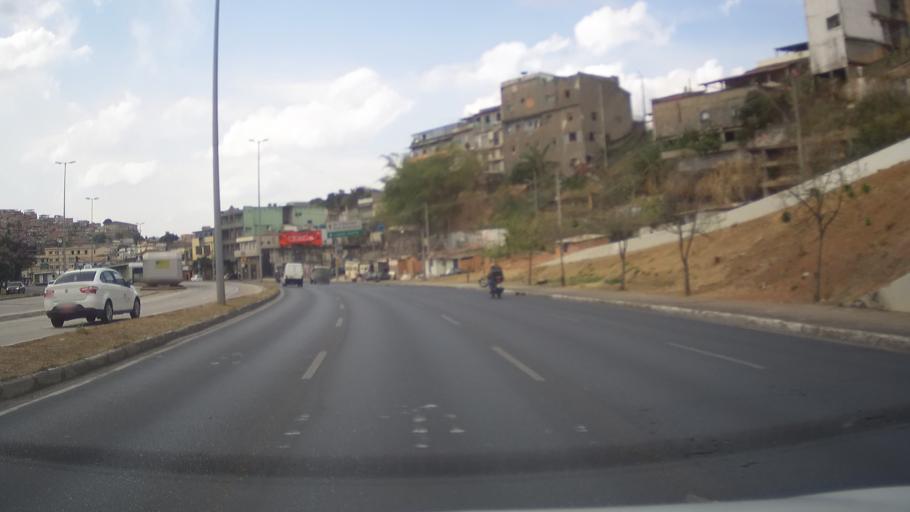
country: BR
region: Minas Gerais
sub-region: Belo Horizonte
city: Belo Horizonte
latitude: -19.8908
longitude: -43.9496
